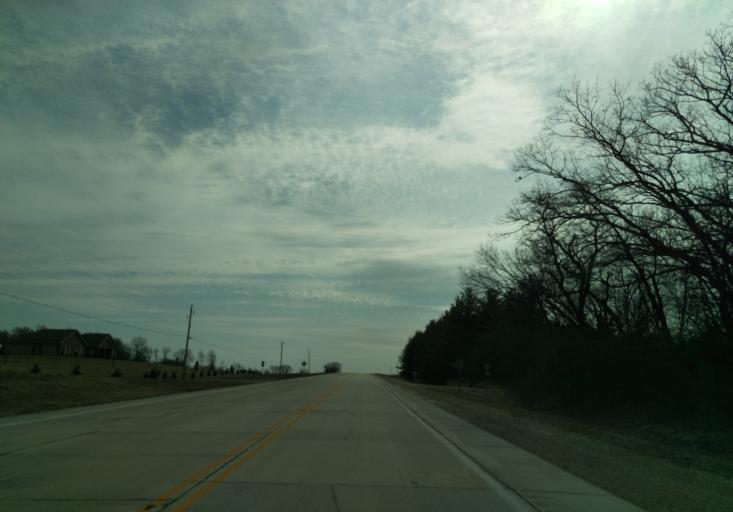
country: US
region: Iowa
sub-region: Winneshiek County
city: Decorah
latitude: 43.3375
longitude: -91.8121
